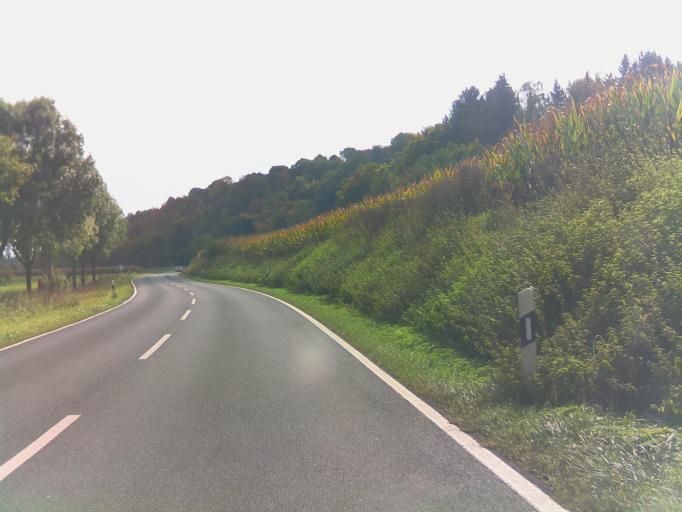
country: DE
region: Bavaria
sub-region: Regierungsbezirk Unterfranken
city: Buchbrunn
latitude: 49.7621
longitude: 10.1512
